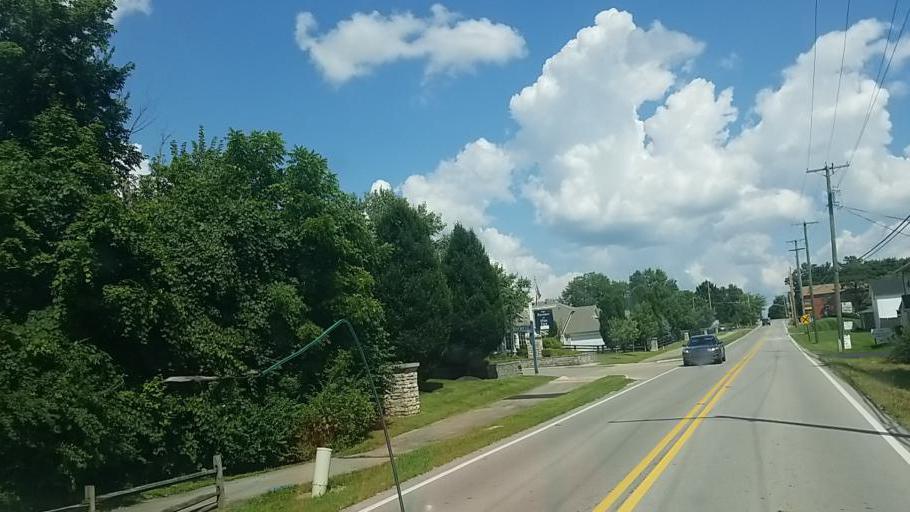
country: US
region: Ohio
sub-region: Franklin County
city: Worthington
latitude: 40.1274
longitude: -83.0079
